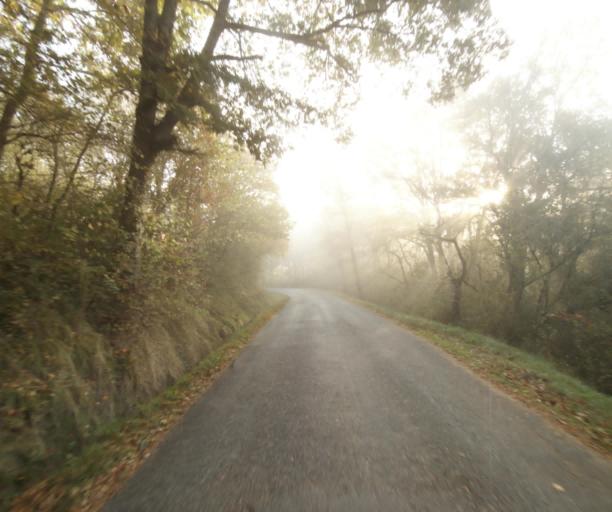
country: FR
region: Midi-Pyrenees
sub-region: Departement de la Haute-Garonne
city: Villemur-sur-Tarn
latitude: 43.8885
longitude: 1.4931
